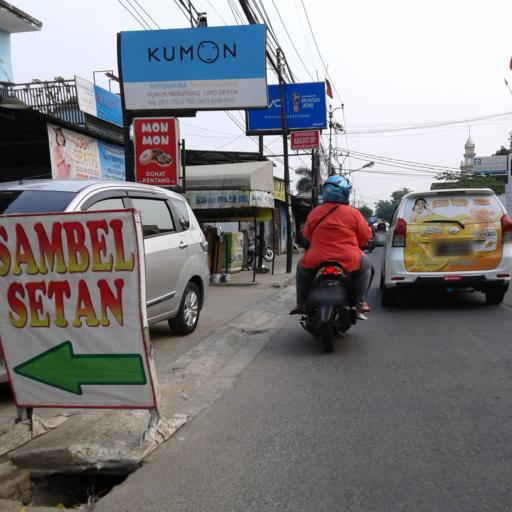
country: ID
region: West Java
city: Sawangan
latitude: -6.3810
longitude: 106.7692
